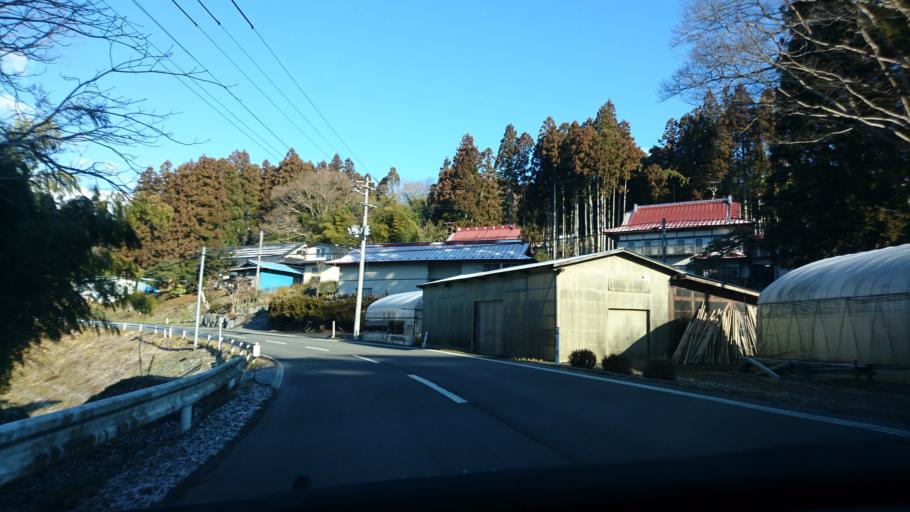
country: JP
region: Iwate
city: Ichinoseki
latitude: 38.8616
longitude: 141.2990
